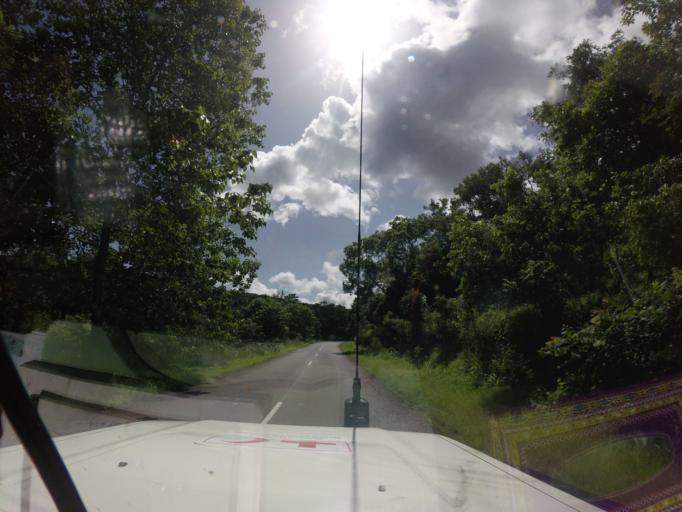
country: GN
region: Mamou
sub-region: Mamou Prefecture
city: Mamou
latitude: 10.2356
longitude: -11.8710
